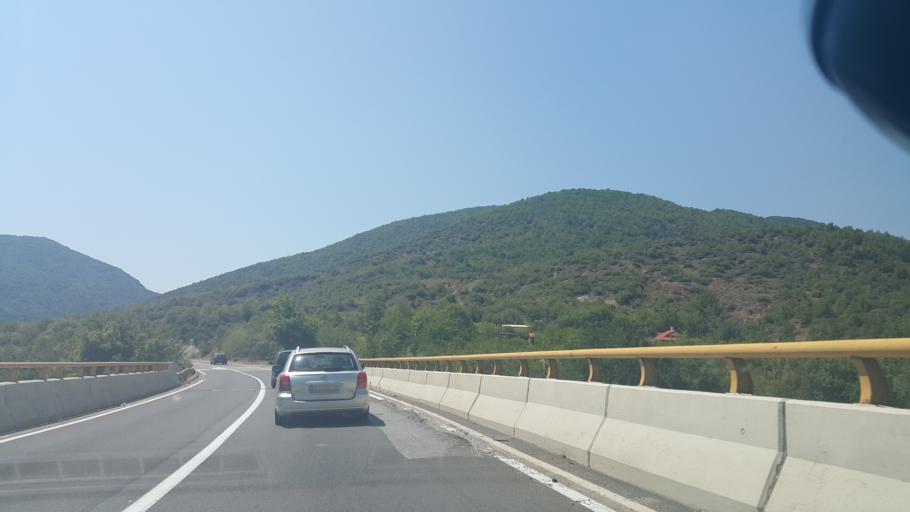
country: MK
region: Gevgelija
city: Miravci
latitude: 41.3791
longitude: 22.4010
